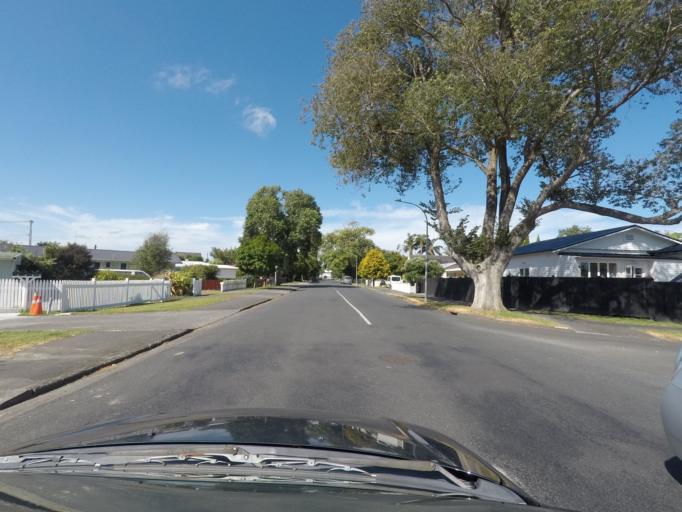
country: NZ
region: Auckland
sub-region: Auckland
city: Rosebank
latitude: -36.8855
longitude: 174.6802
